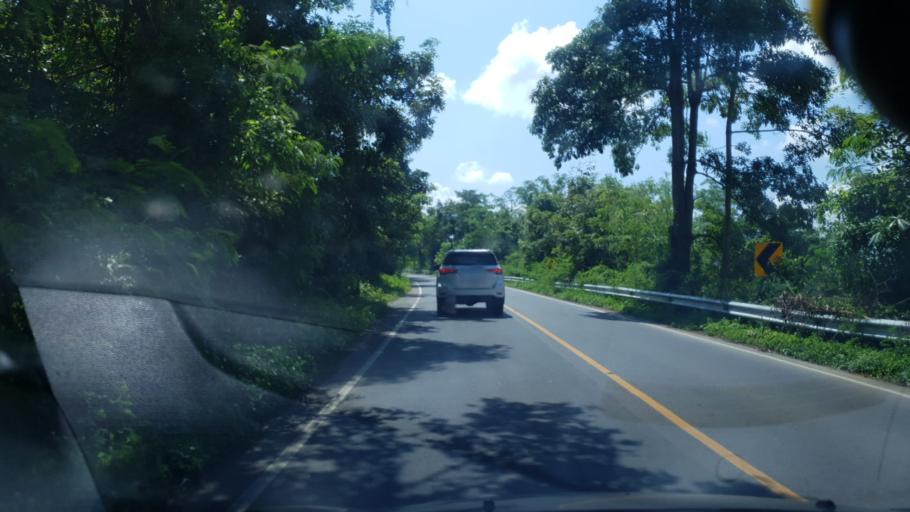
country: TH
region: Chiang Rai
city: Wiang Chai
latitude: 19.9430
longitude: 99.9198
